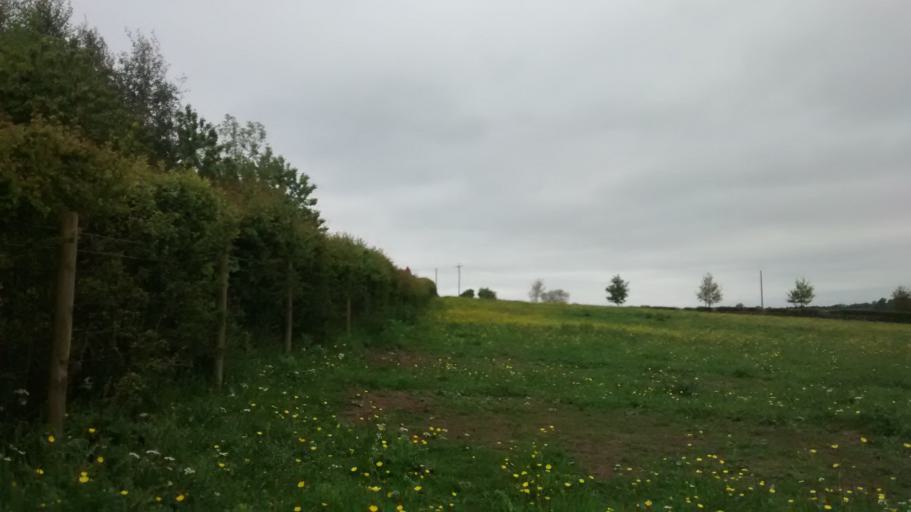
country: GB
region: England
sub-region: County Durham
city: Pittington
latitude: 54.7833
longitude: -1.5049
